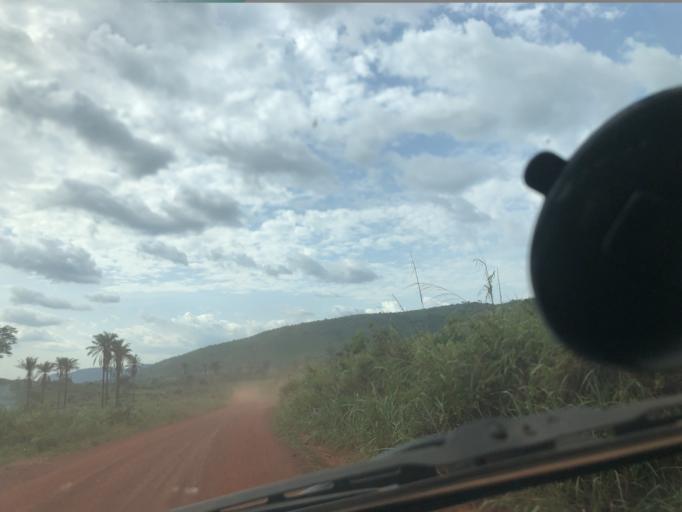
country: CF
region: Bangui
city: Bangui
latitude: 4.3047
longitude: 18.6161
